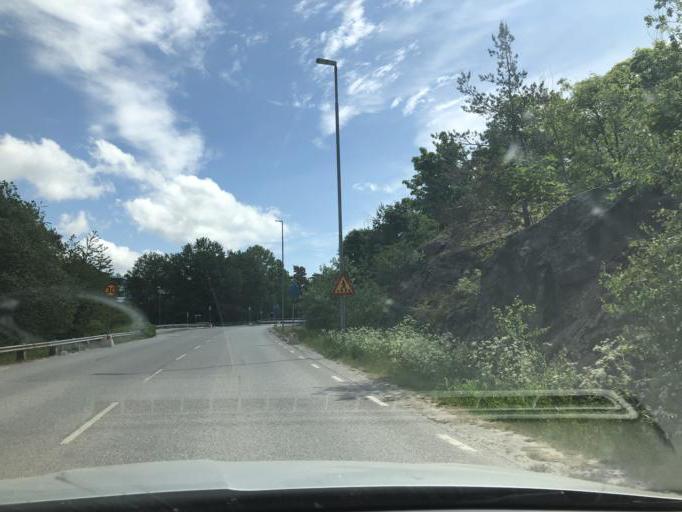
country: SE
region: Stockholm
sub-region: Botkyrka Kommun
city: Alby
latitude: 59.2428
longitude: 17.8525
